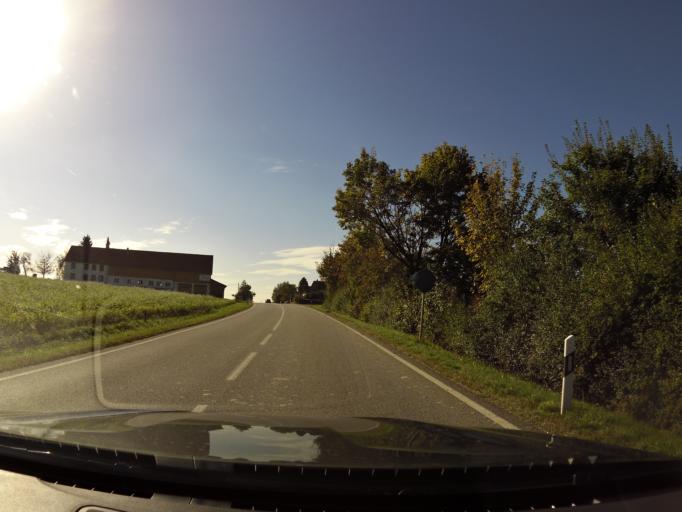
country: DE
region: Bavaria
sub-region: Lower Bavaria
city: Vilsheim
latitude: 48.4314
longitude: 12.1394
